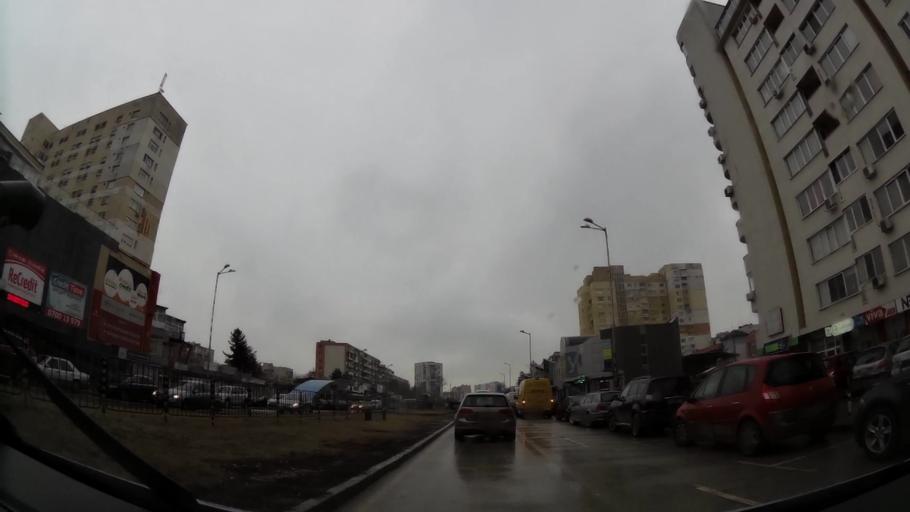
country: BG
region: Sofia-Capital
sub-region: Stolichna Obshtina
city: Sofia
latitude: 42.6532
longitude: 23.3728
